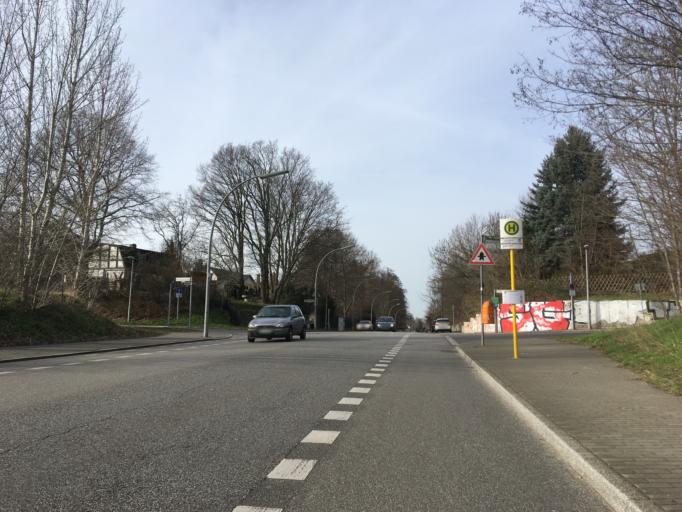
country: DE
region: Berlin
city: Lubars
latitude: 52.6119
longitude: 13.3587
